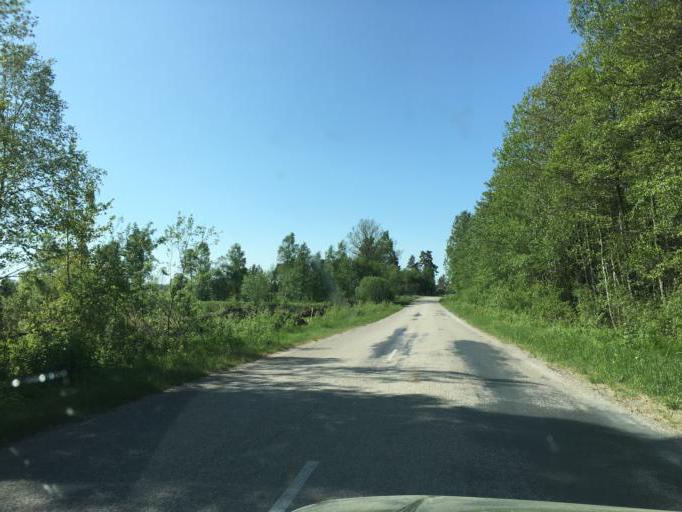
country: LV
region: Ventspils
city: Ventspils
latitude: 57.5058
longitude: 21.8481
